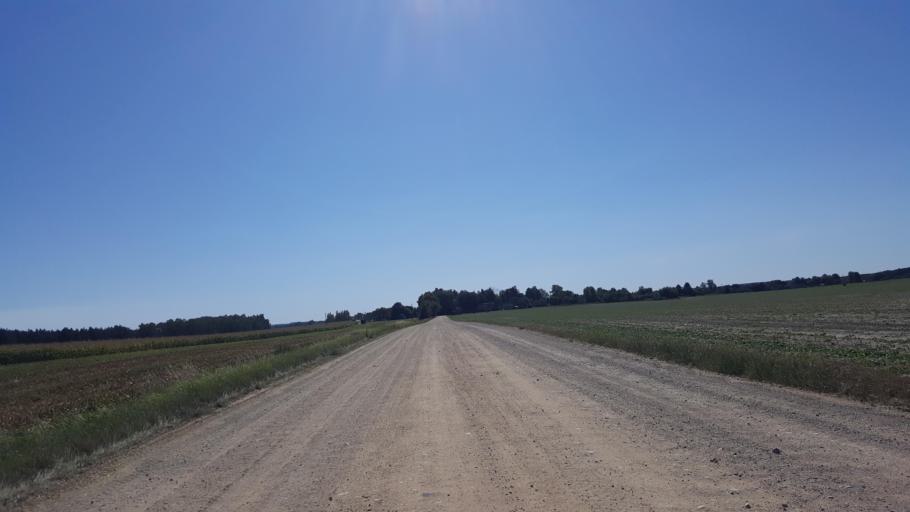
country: PL
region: Lublin Voivodeship
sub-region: Powiat bialski
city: Rokitno
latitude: 52.2194
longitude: 23.3983
